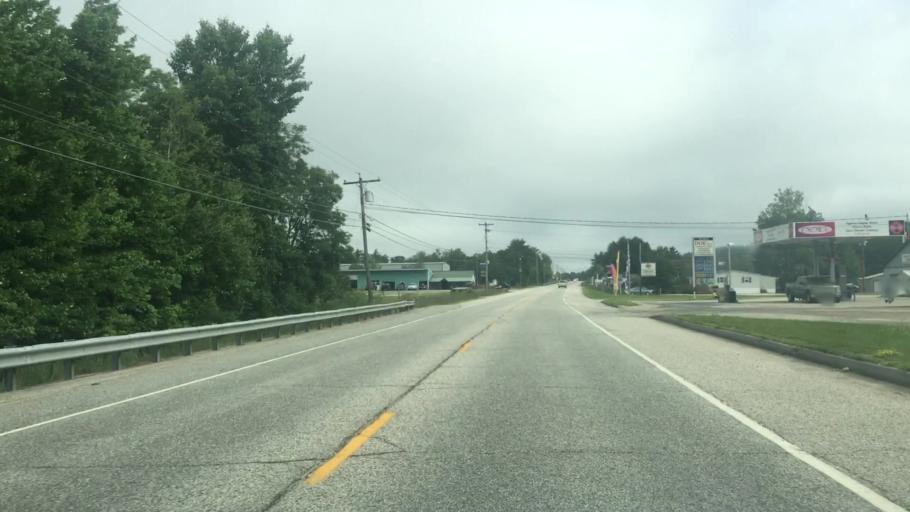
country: US
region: Maine
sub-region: Oxford County
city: South Paris
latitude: 44.2364
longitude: -70.5139
